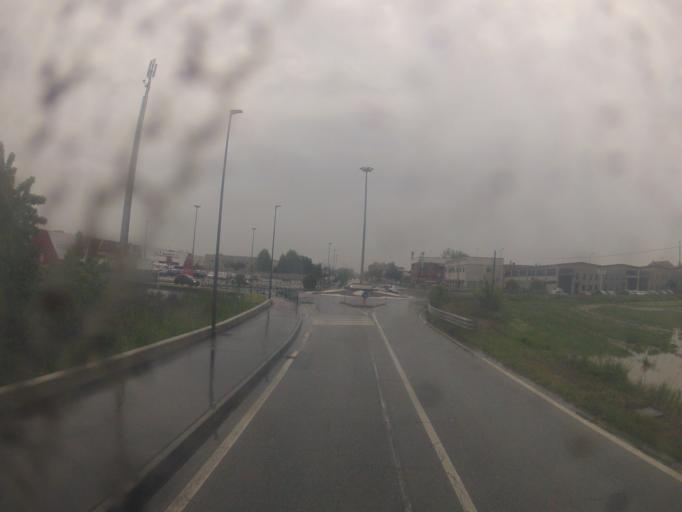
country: IT
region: Piedmont
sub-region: Provincia di Torino
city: La Loggia
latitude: 44.9457
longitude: 7.6697
